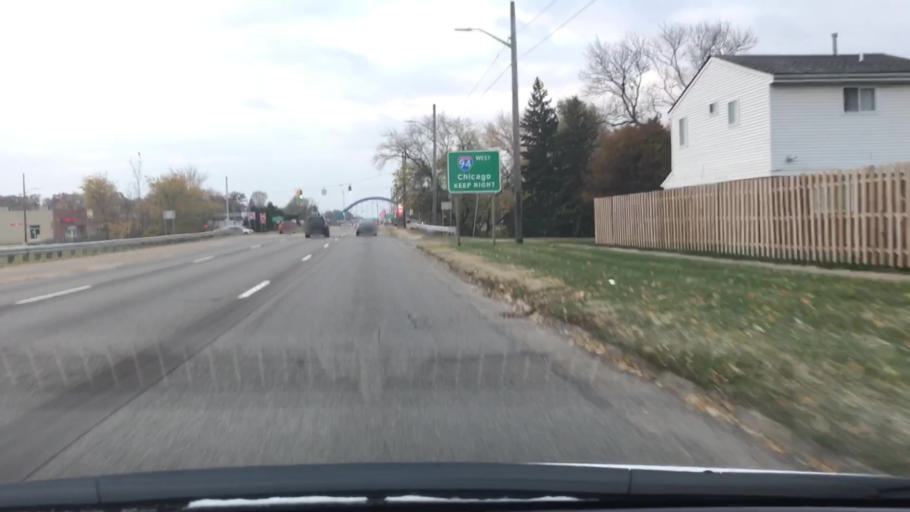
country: US
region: Michigan
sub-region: Wayne County
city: Taylor
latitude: 42.2723
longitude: -83.2707
